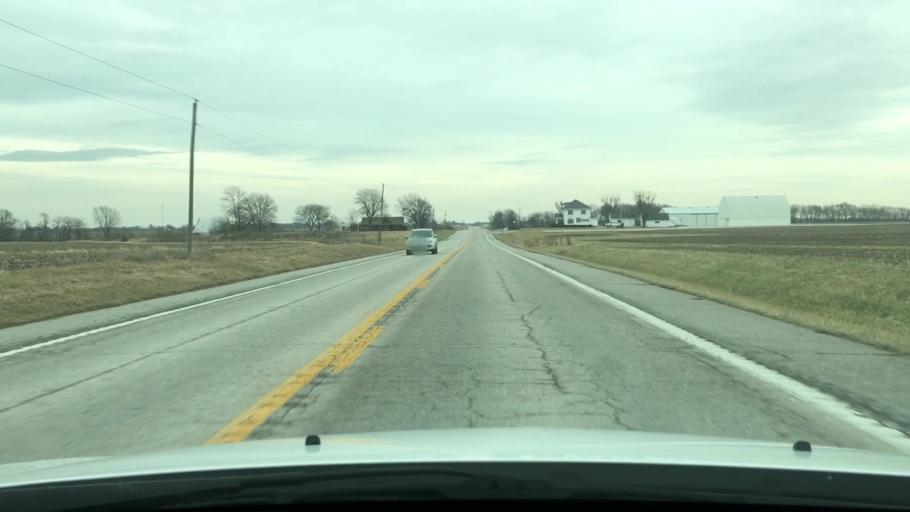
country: US
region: Missouri
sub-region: Audrain County
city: Vandalia
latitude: 39.2805
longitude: -91.6217
